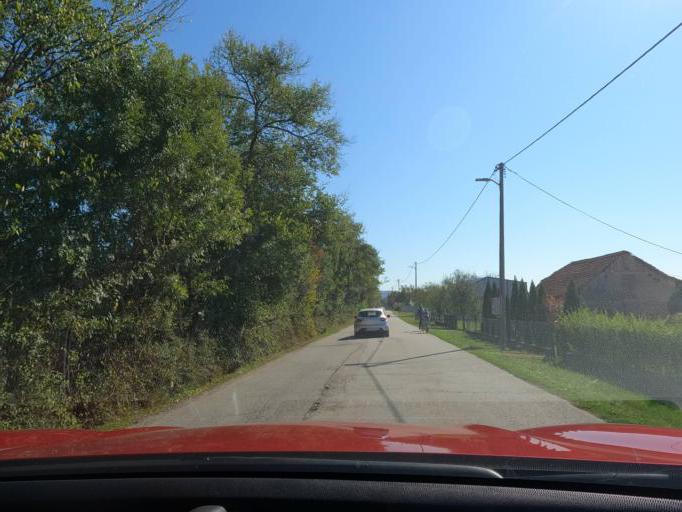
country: RS
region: Central Serbia
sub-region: Raski Okrug
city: Kraljevo
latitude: 43.7550
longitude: 20.6930
